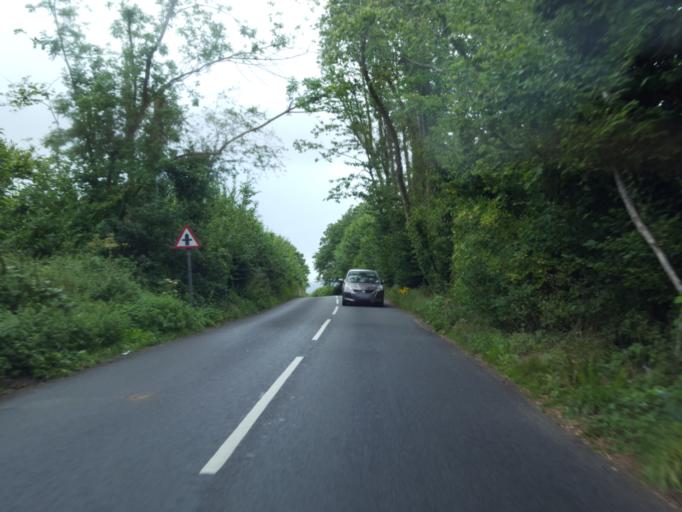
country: GB
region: England
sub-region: Kent
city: Yalding
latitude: 51.2327
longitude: 0.4785
